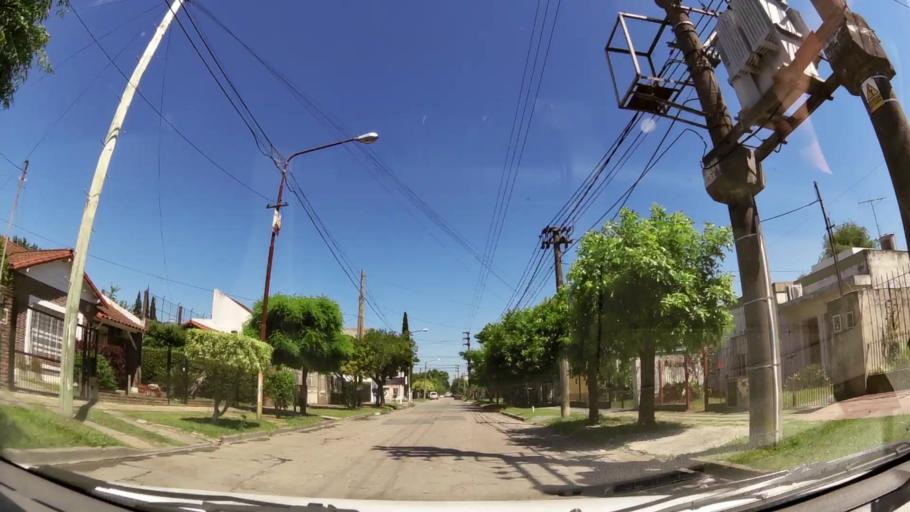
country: AR
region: Buenos Aires
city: Ituzaingo
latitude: -34.6859
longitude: -58.6630
